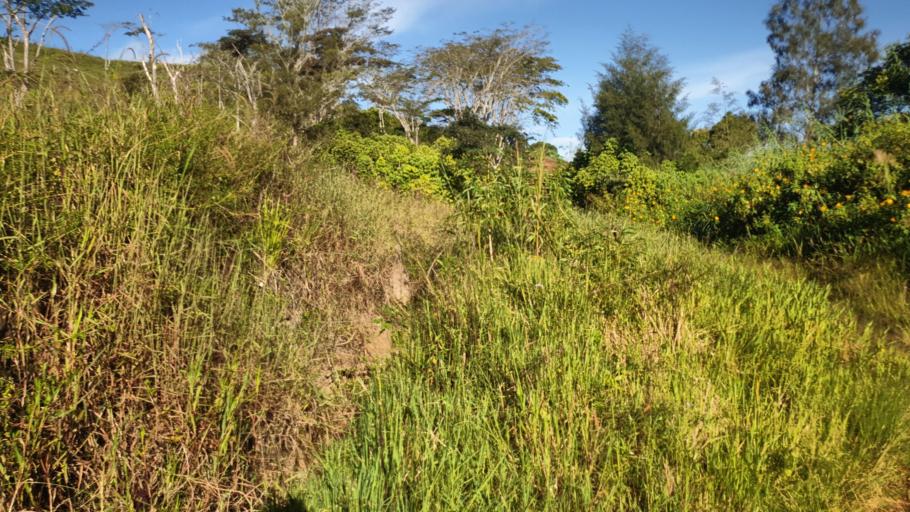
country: PG
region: Western Highlands
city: Rauna
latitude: -5.8003
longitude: 144.3629
